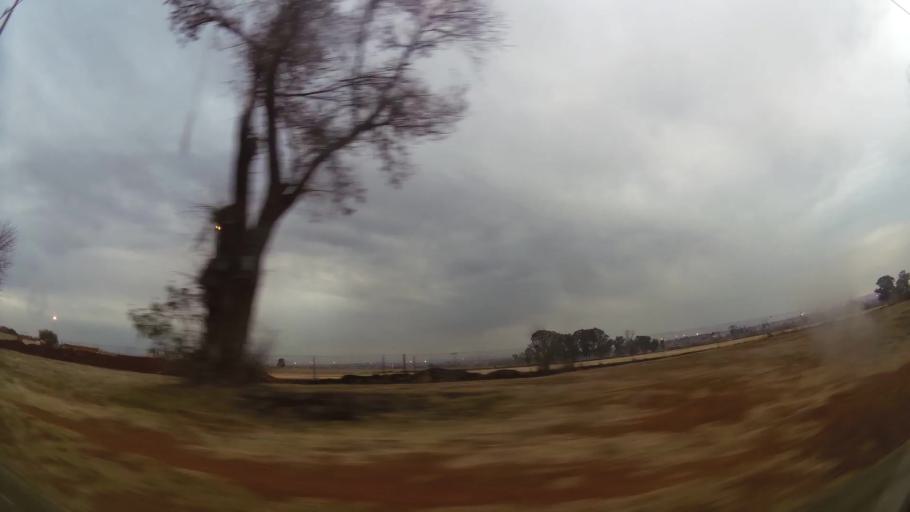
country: ZA
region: Gauteng
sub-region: Ekurhuleni Metropolitan Municipality
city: Germiston
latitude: -26.3503
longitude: 28.1833
